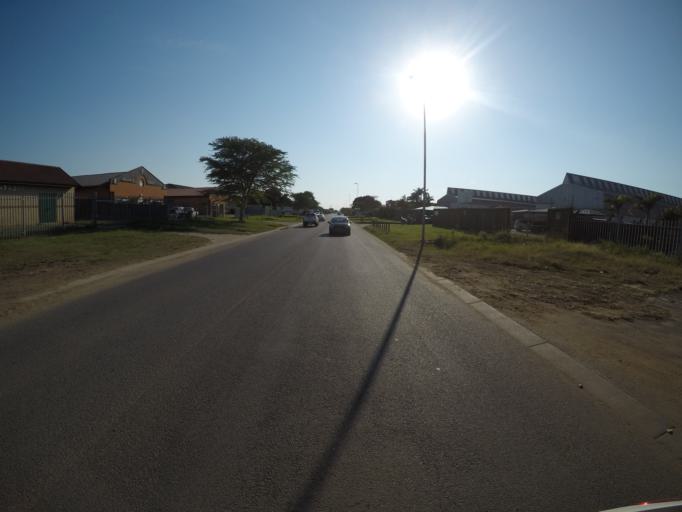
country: ZA
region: KwaZulu-Natal
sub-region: uThungulu District Municipality
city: Richards Bay
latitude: -28.7472
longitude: 32.0344
